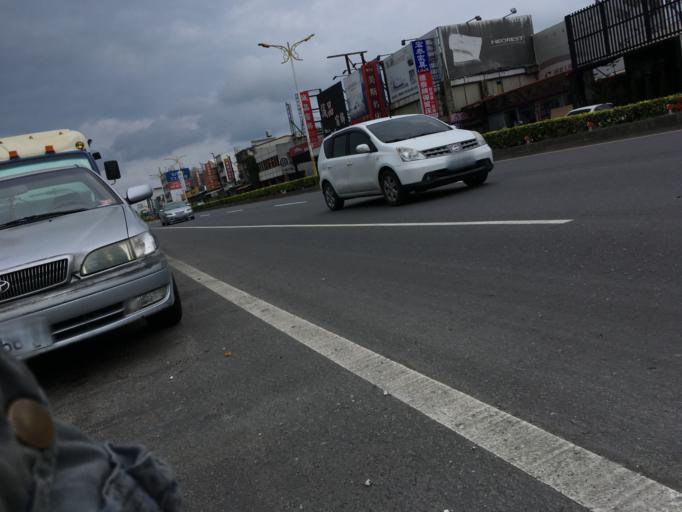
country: TW
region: Taiwan
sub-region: Hualien
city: Hualian
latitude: 23.9980
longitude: 121.5961
